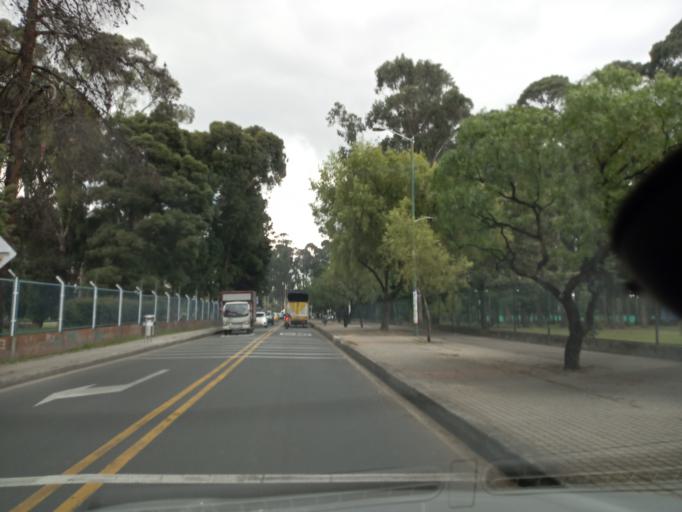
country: CO
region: Bogota D.C.
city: Bogota
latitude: 4.5712
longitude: -74.1056
